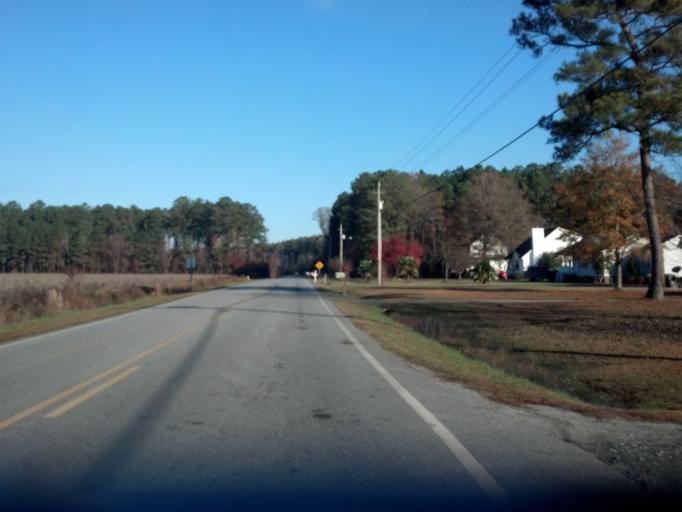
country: US
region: North Carolina
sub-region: Pitt County
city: Winterville
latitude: 35.5357
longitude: -77.4418
